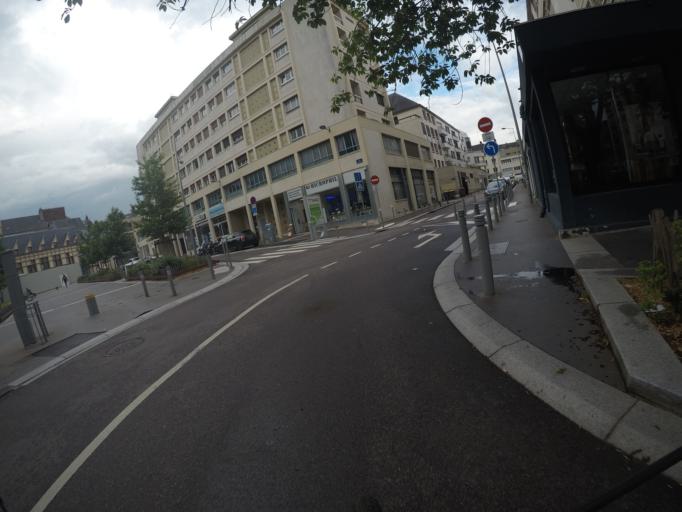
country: FR
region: Haute-Normandie
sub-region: Departement de la Seine-Maritime
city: Rouen
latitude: 49.4413
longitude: 1.0874
